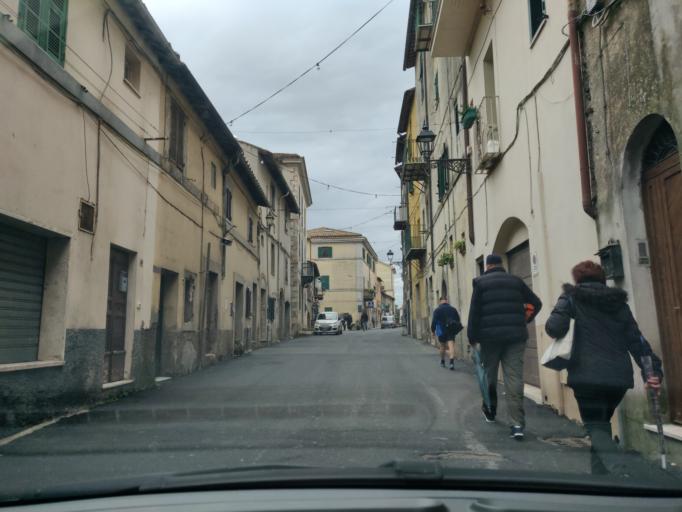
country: IT
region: Latium
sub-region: Citta metropolitana di Roma Capitale
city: Tolfa
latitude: 42.1522
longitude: 11.9406
